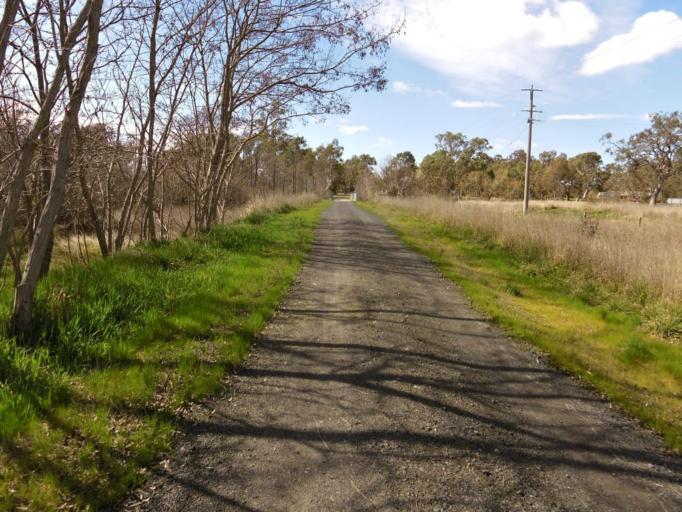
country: AU
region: Victoria
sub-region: Mansfield
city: Mansfield
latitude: -37.0473
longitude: 146.0589
